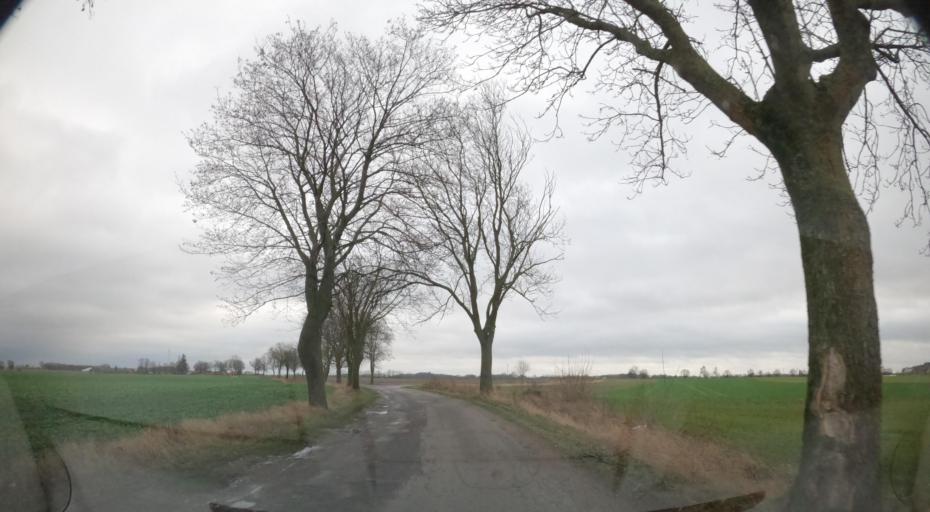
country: PL
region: Greater Poland Voivodeship
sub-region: Powiat pilski
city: Wysoka
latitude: 53.2658
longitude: 17.1112
